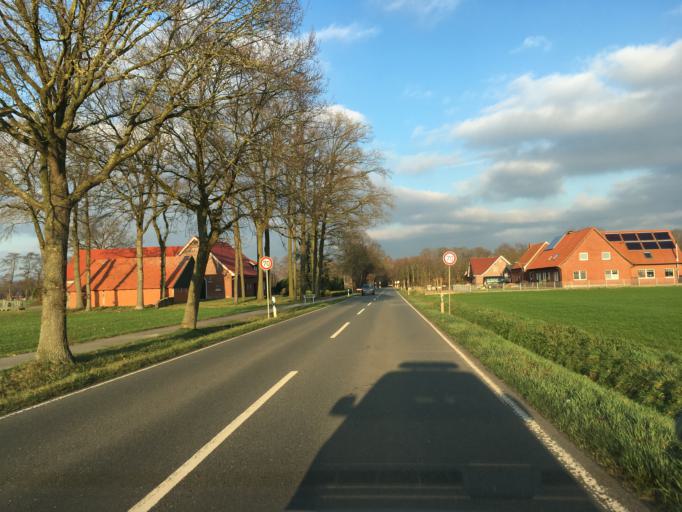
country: DE
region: North Rhine-Westphalia
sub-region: Regierungsbezirk Munster
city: Gronau
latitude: 52.1591
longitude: 7.0250
